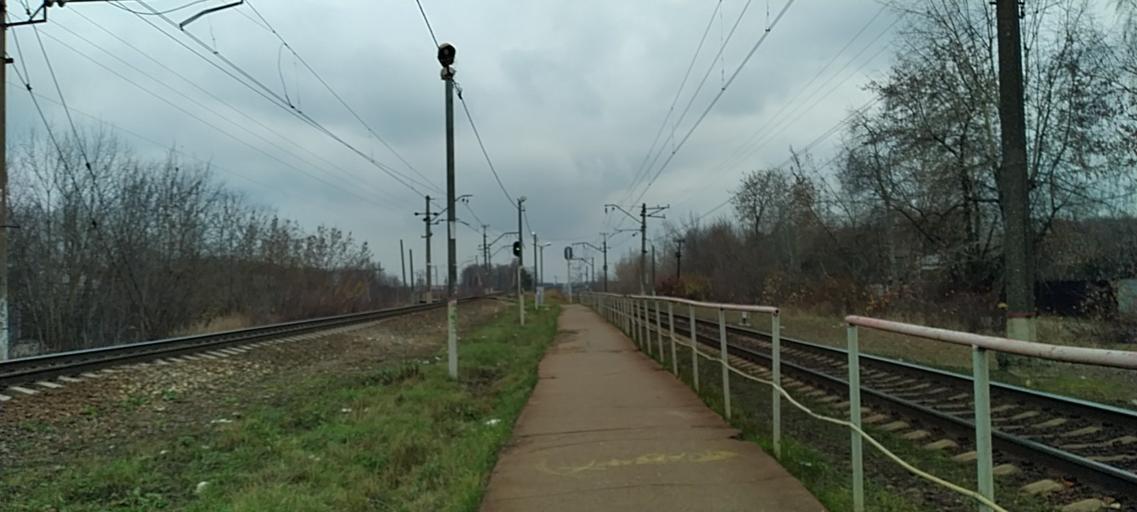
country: RU
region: Moskovskaya
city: Korenevo
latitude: 55.6679
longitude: 38.0028
